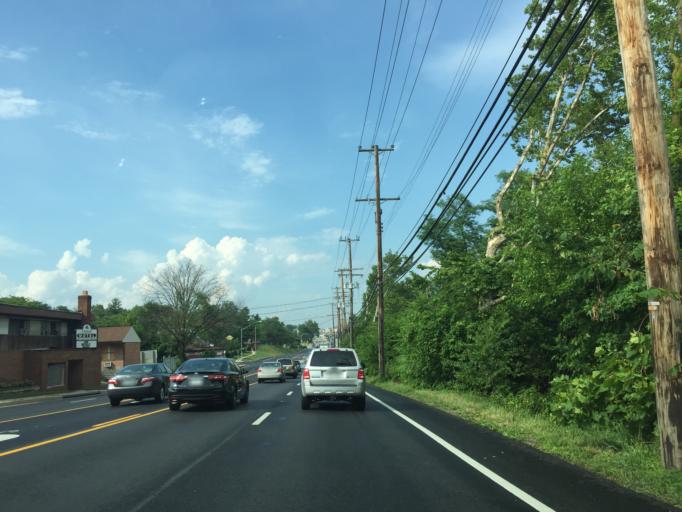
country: US
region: Maryland
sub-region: Anne Arundel County
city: Jessup
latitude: 39.1663
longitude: -76.7903
